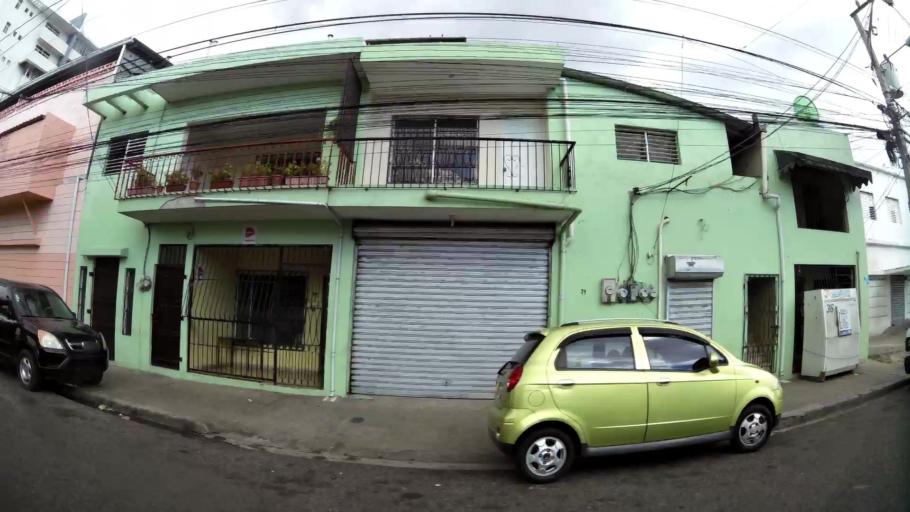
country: DO
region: Nacional
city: San Carlos
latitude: 18.4889
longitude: -69.9168
